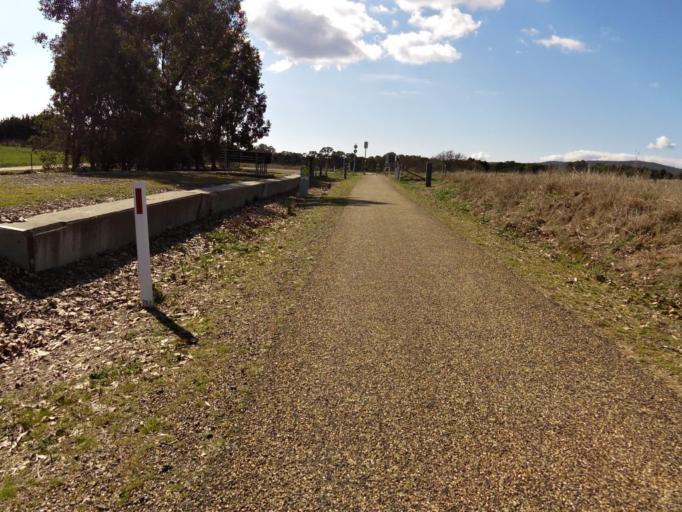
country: AU
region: Victoria
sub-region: Wangaratta
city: Wangaratta
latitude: -36.3951
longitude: 146.6572
